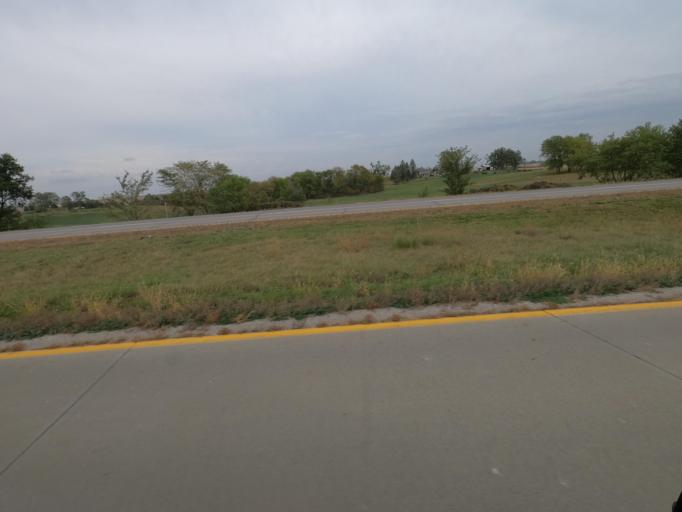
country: US
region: Iowa
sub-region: Marion County
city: Pella
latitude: 41.4232
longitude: -92.9678
